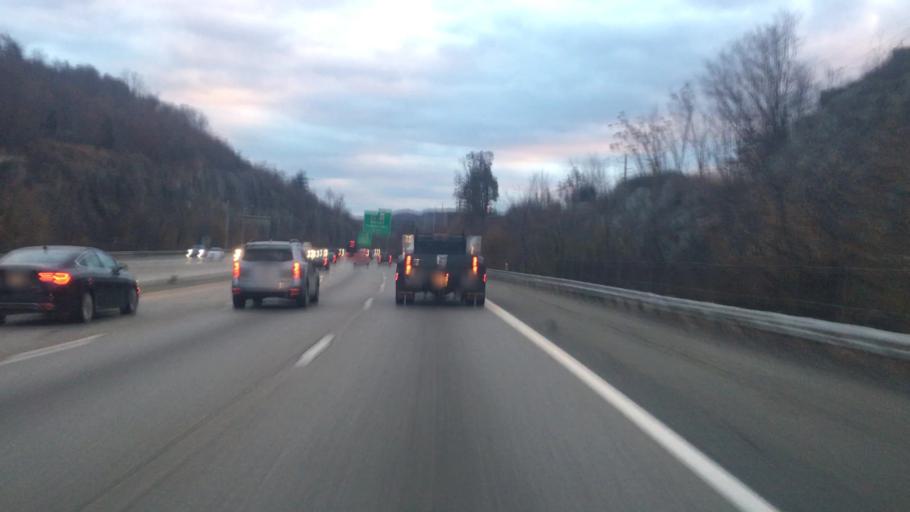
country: US
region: New Jersey
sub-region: Passaic County
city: Wanaque
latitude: 41.0238
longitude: -74.2908
